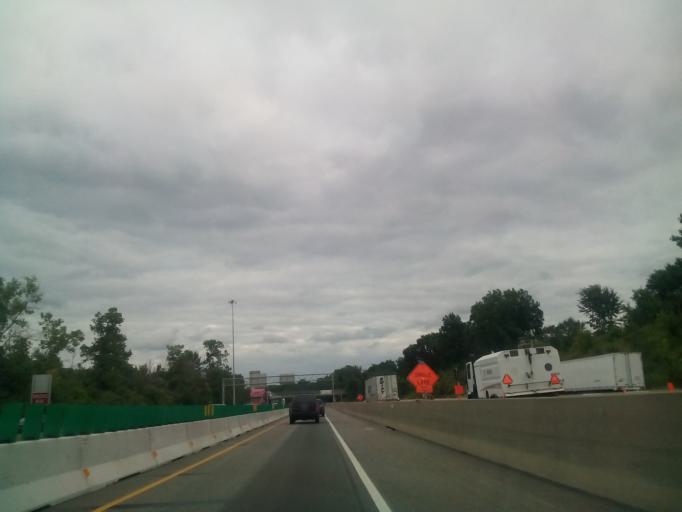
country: US
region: Ohio
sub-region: Lorain County
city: Elyria
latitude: 41.3866
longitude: -82.1091
